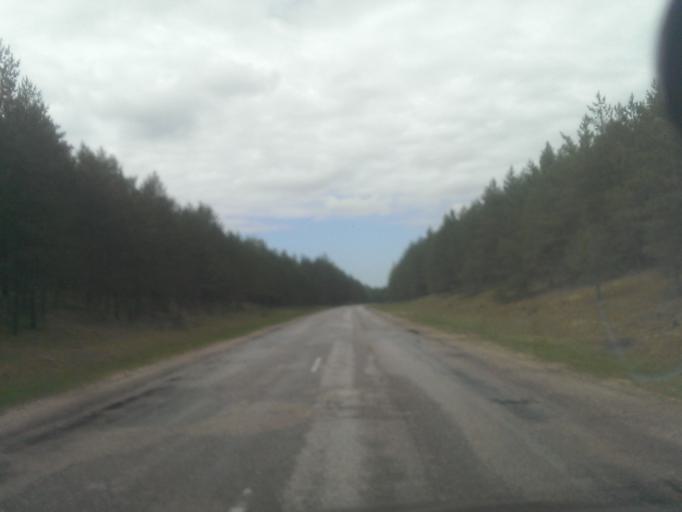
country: LV
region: Ventspils Rajons
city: Piltene
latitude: 57.1155
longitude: 21.7537
